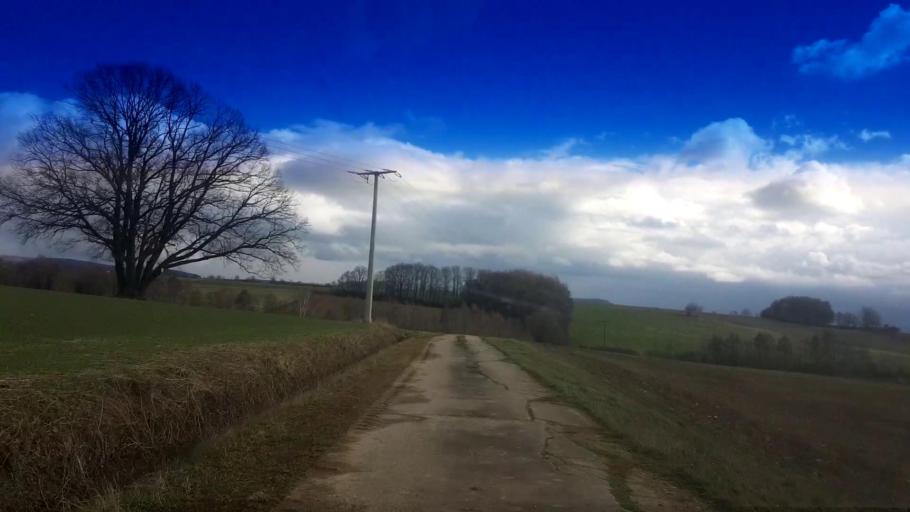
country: DE
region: Bavaria
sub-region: Upper Franconia
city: Schesslitz
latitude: 49.9916
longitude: 11.0177
